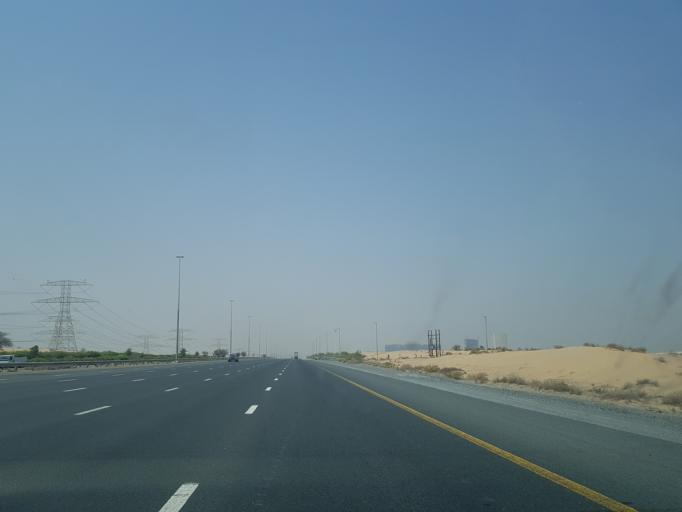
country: AE
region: Ash Shariqah
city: Sharjah
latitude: 25.1035
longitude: 55.4150
